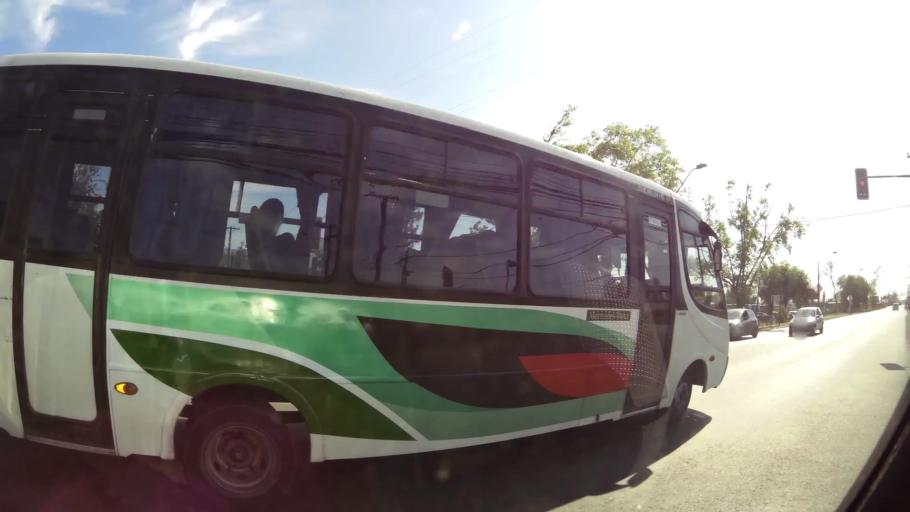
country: CL
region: Santiago Metropolitan
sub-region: Provincia de Talagante
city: Talagante
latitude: -33.6744
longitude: -70.9505
